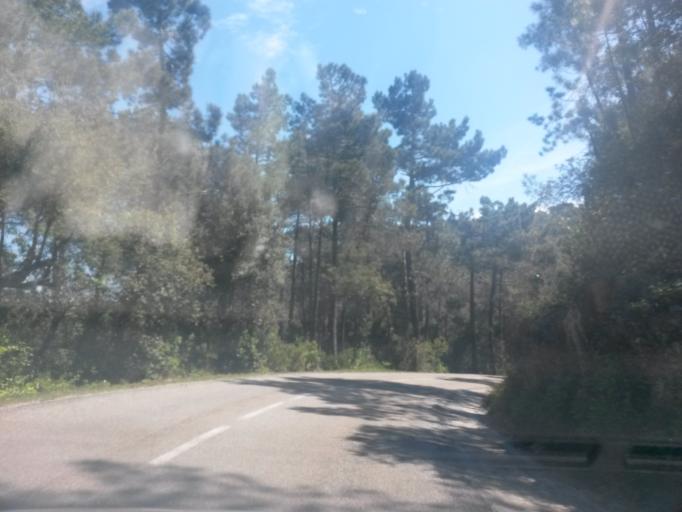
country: ES
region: Catalonia
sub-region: Provincia de Girona
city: Madremanya
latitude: 41.9834
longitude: 2.9459
